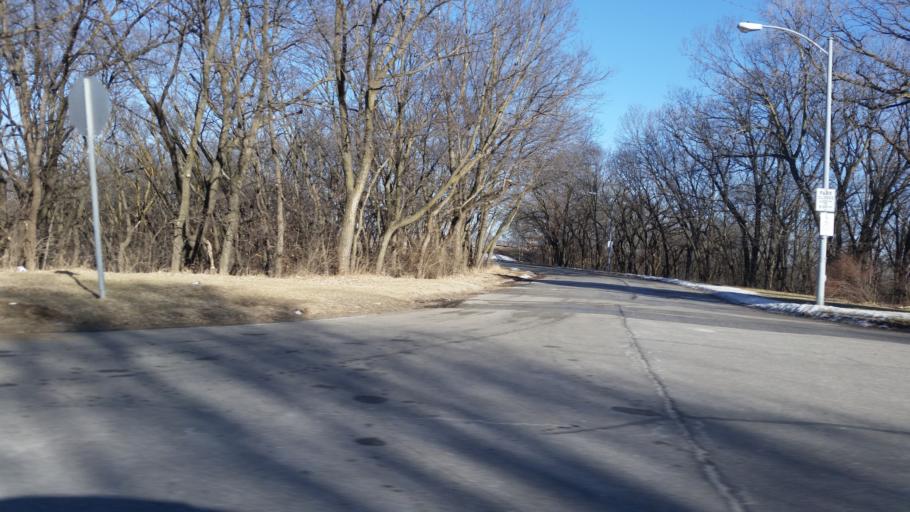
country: US
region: Nebraska
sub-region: Douglas County
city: Omaha
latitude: 41.1959
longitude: -95.9335
